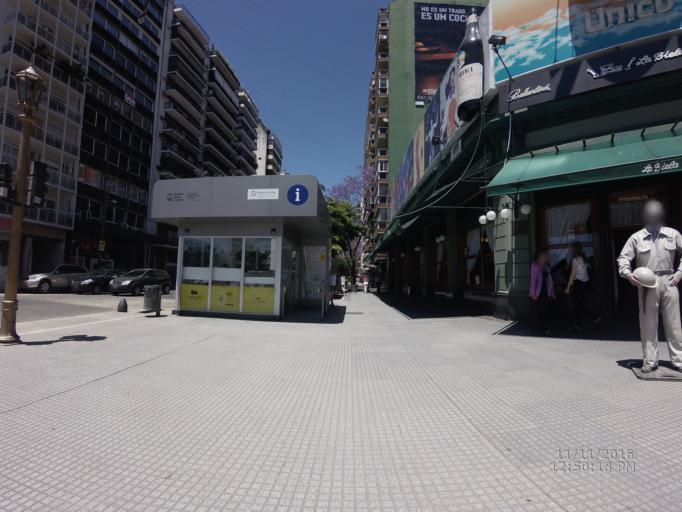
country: AR
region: Buenos Aires F.D.
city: Retiro
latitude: -34.5878
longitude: -58.3909
